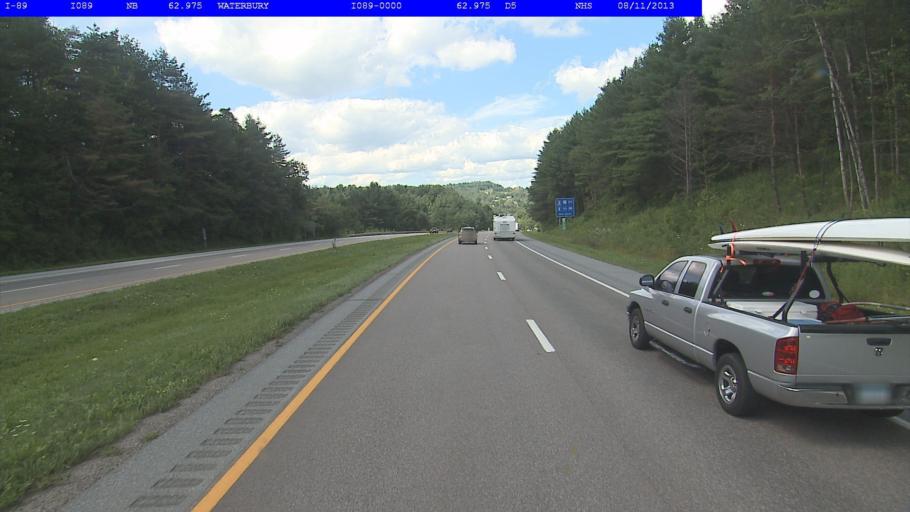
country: US
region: Vermont
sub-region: Washington County
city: Waterbury
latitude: 44.3335
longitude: -72.7461
